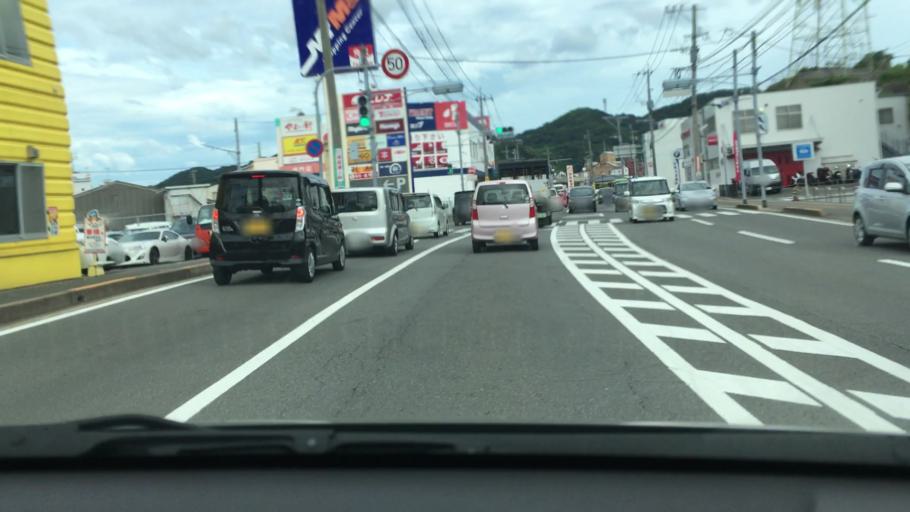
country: JP
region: Nagasaki
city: Togitsu
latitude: 32.8333
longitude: 129.8439
